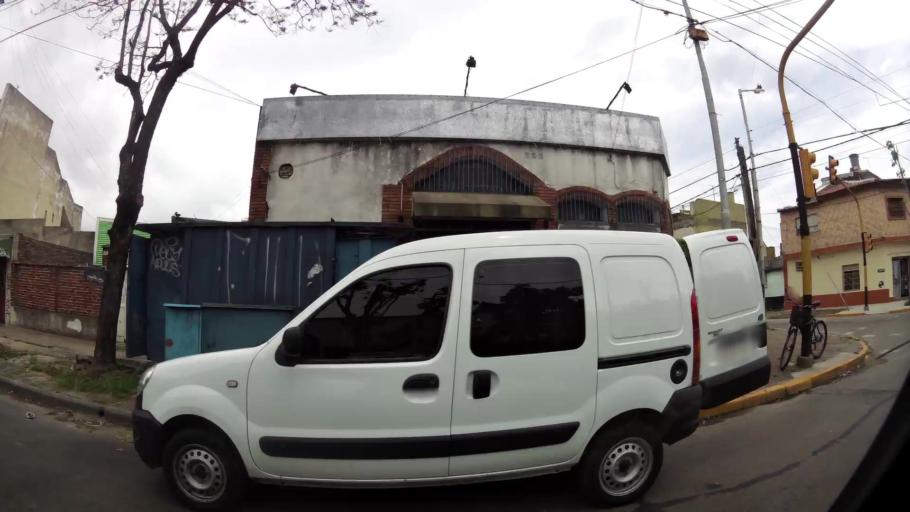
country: AR
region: Buenos Aires
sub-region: Partido de Avellaneda
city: Avellaneda
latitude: -34.6820
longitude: -58.3766
